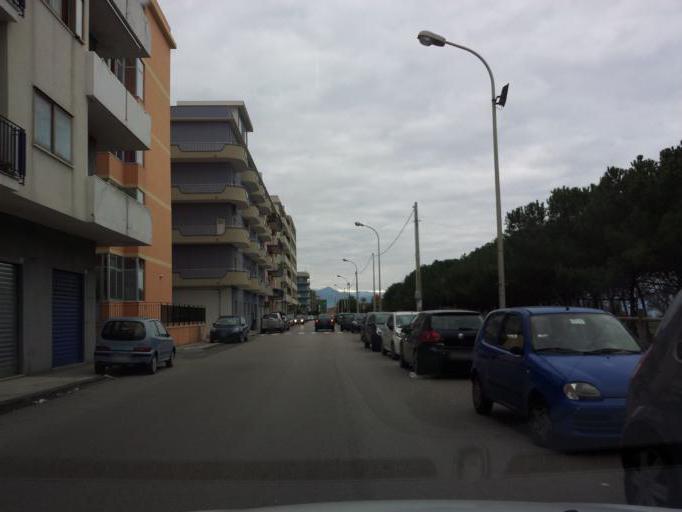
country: IT
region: Sicily
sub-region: Messina
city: Milazzo
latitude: 38.2262
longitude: 15.2361
